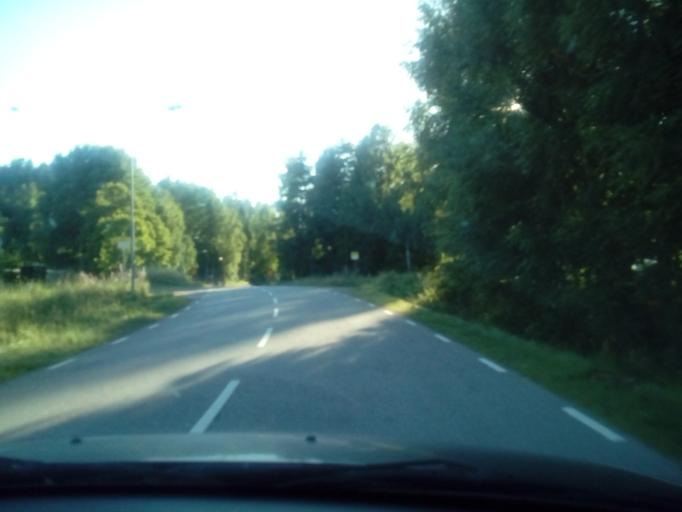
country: SE
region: Kalmar
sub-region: Vasterviks Kommun
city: Ankarsrum
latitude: 57.7853
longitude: 16.2672
